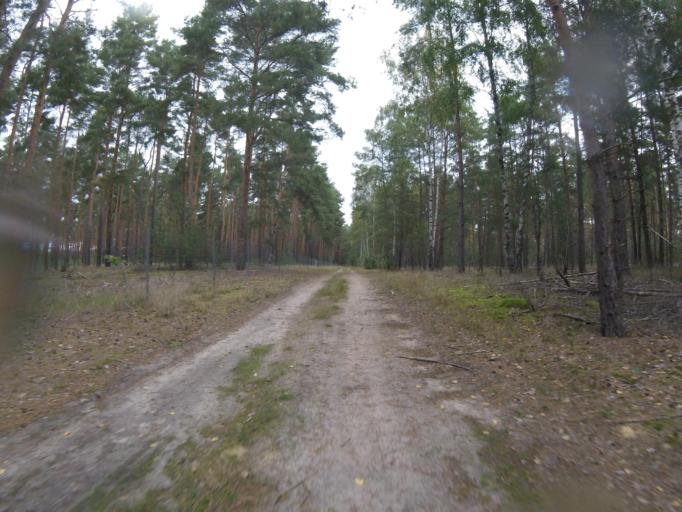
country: DE
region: Brandenburg
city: Gross Koris
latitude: 52.1824
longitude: 13.6773
